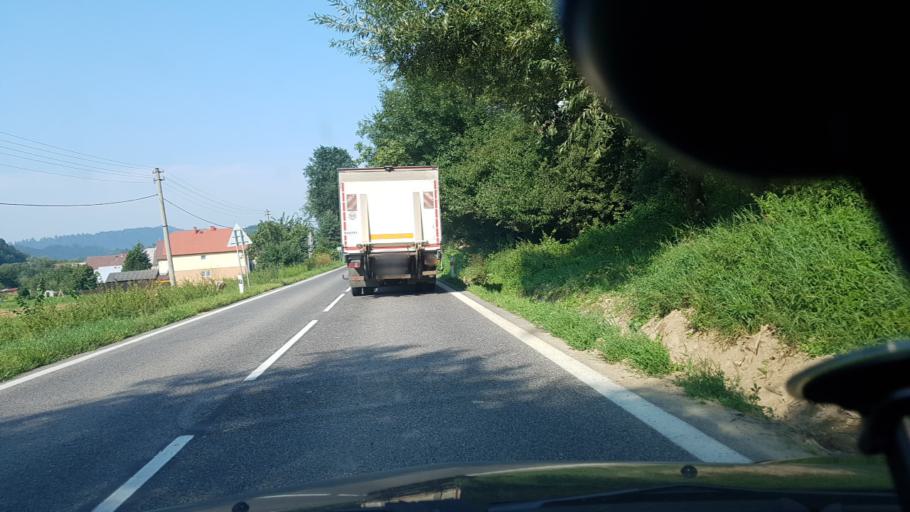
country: SK
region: Zilinsky
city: Tvrdosin
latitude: 49.2672
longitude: 19.4553
